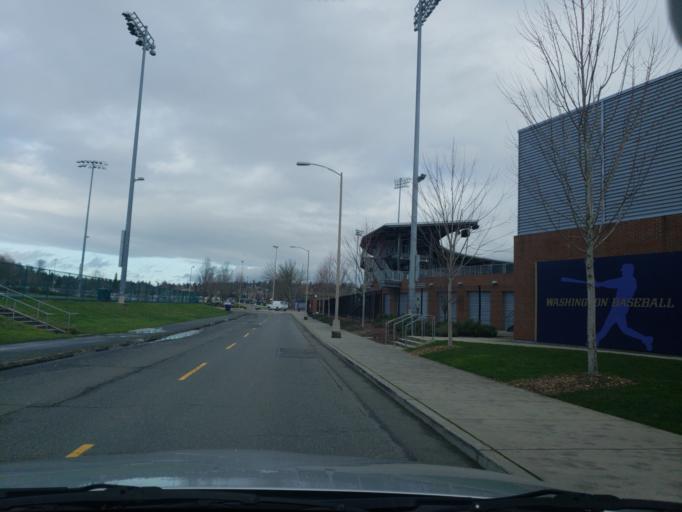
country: US
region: Washington
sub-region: King County
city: Seattle
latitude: 47.6544
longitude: -122.2999
